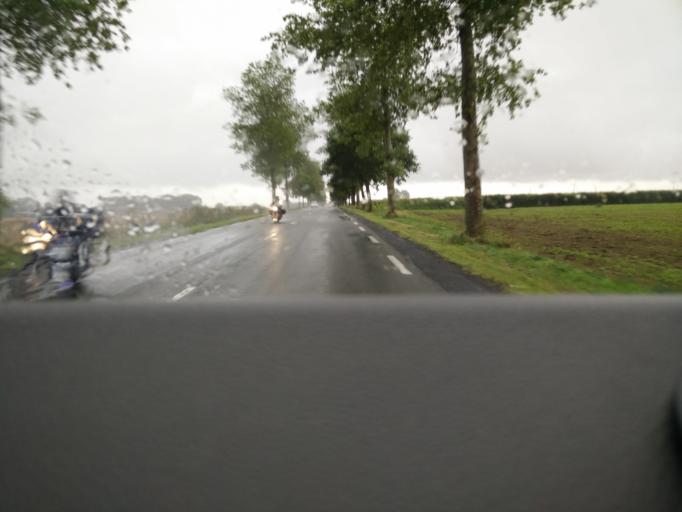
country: FR
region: Nord-Pas-de-Calais
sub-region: Departement du Pas-de-Calais
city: Savy-Berlette
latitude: 50.3584
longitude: 2.4663
